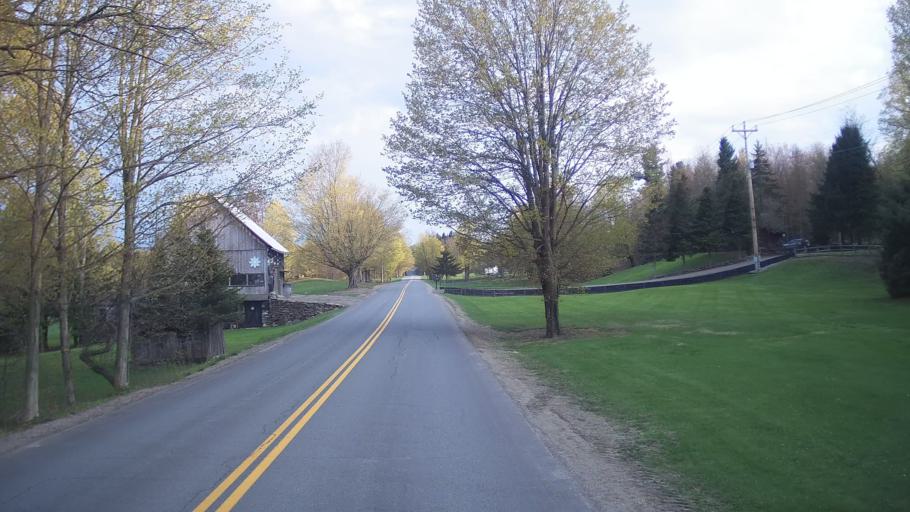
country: US
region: Vermont
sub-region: Orleans County
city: Newport
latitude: 44.9184
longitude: -72.4314
